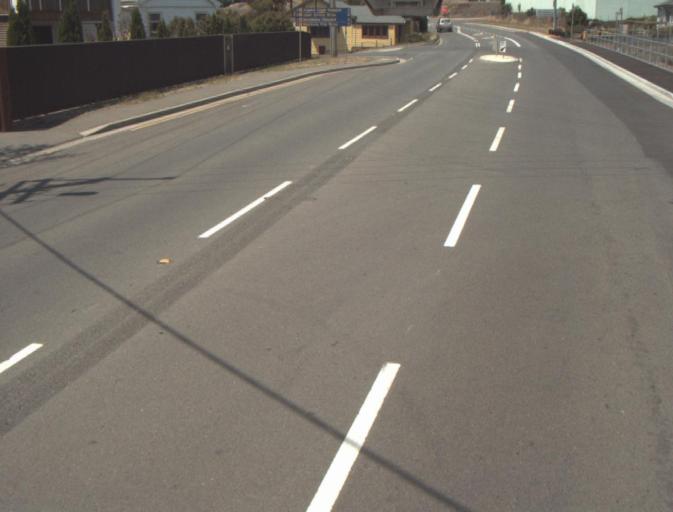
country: AU
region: Tasmania
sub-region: Launceston
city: Summerhill
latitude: -41.4912
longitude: 147.1681
